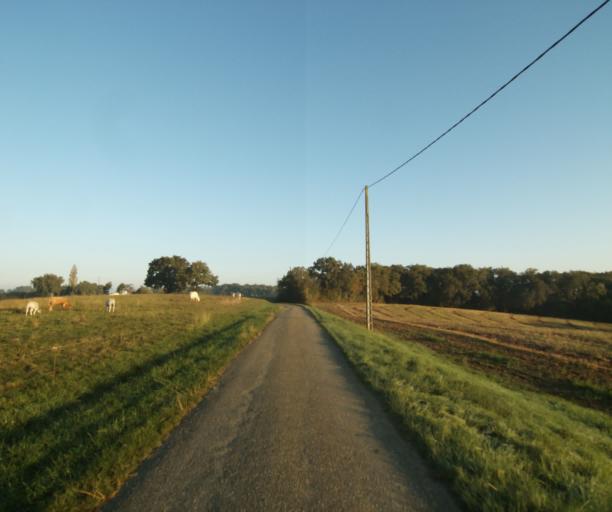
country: FR
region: Midi-Pyrenees
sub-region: Departement du Gers
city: Vic-Fezensac
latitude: 43.7702
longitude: 0.1926
